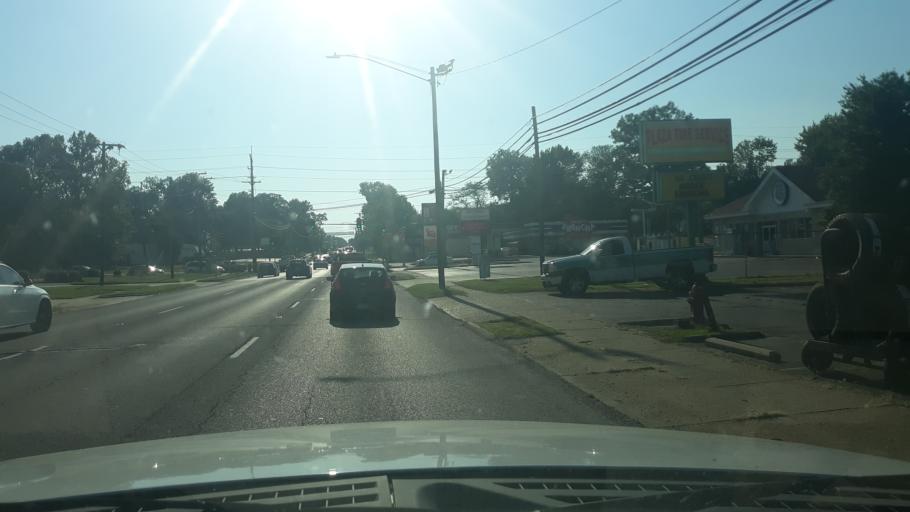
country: US
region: Illinois
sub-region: Jackson County
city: Carbondale
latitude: 37.7280
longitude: -89.2075
